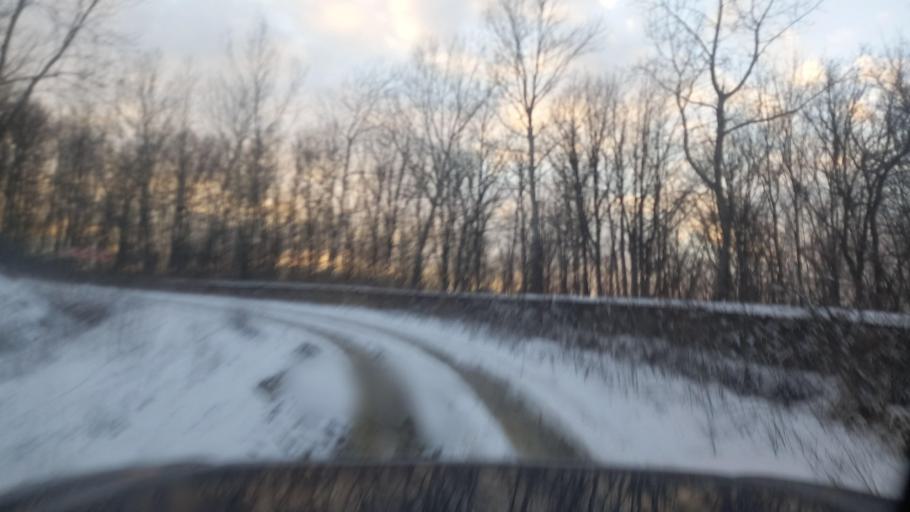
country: RU
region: Krasnodarskiy
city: Smolenskaya
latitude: 44.6729
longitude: 38.7881
